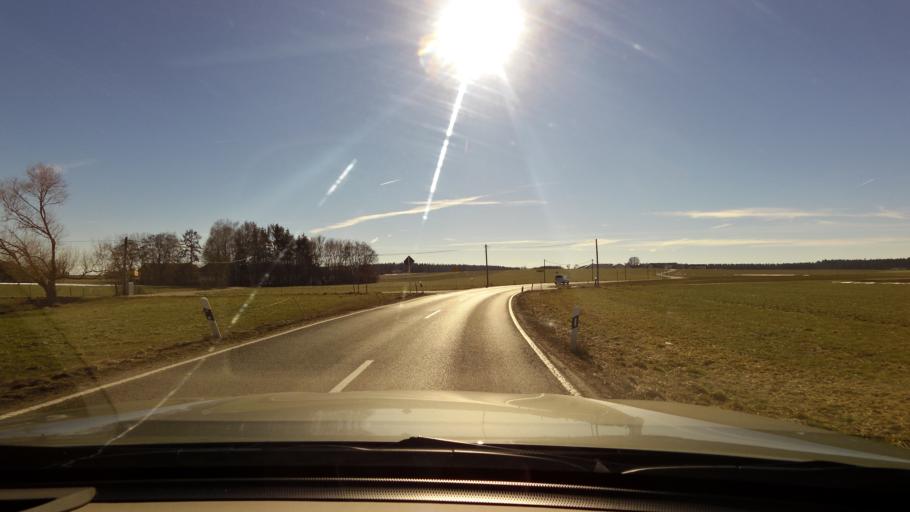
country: DE
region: Bavaria
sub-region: Upper Bavaria
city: Taufkirchen
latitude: 48.1696
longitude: 12.4610
